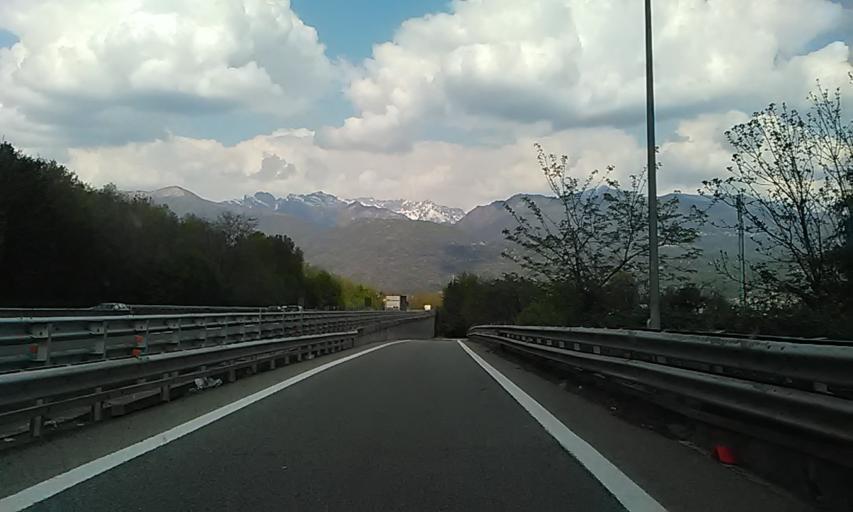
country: IT
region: Piedmont
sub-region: Provincia Verbano-Cusio-Ossola
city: Baveno
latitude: 45.9165
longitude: 8.4851
